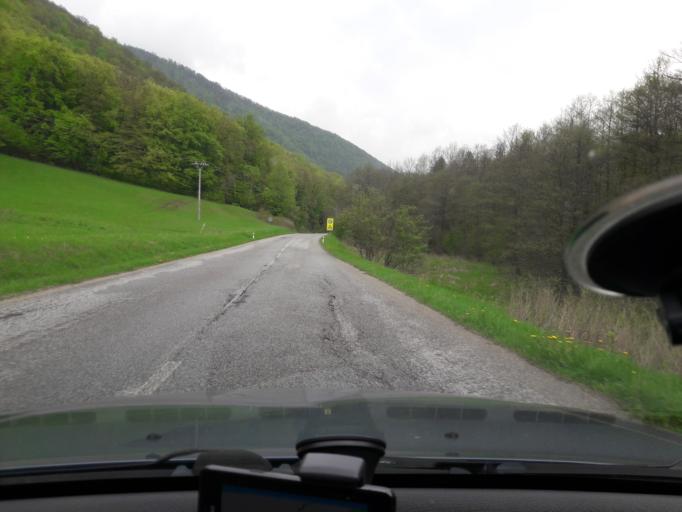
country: SK
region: Banskobystricky
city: Tisovec
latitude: 48.7150
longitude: 20.0029
